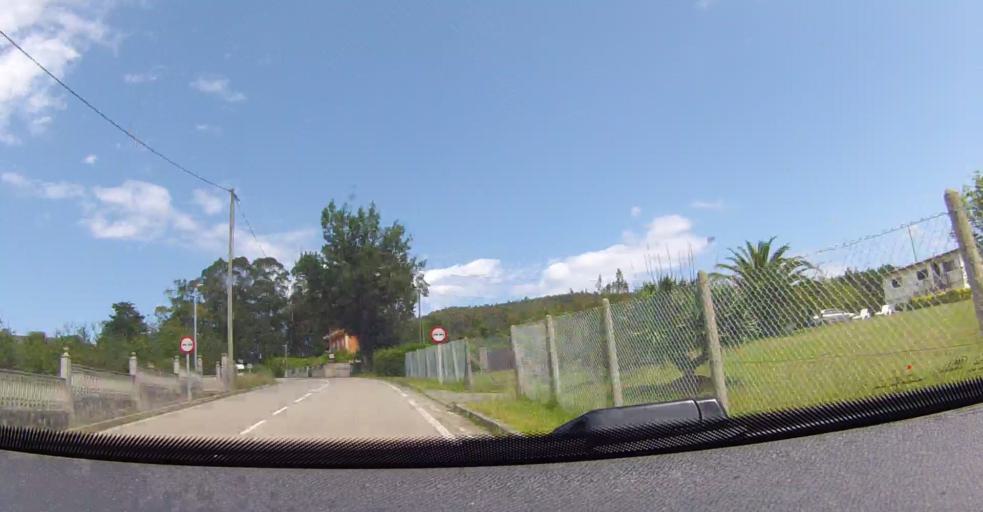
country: ES
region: Asturias
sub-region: Province of Asturias
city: Villaviciosa
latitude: 43.5295
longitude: -5.3730
